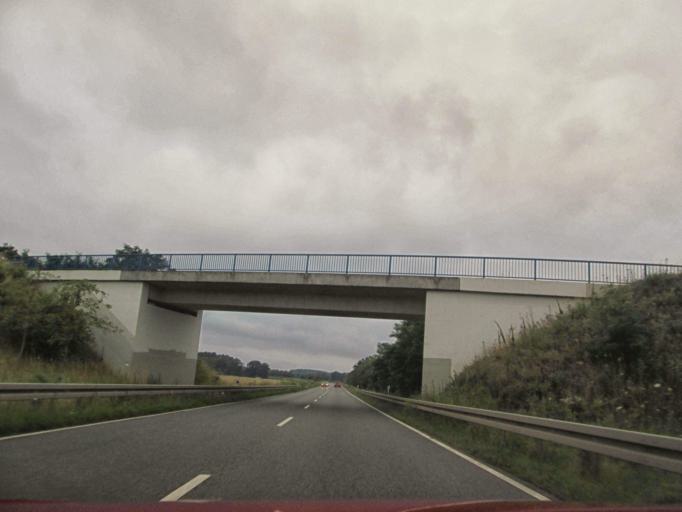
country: DE
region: Lower Saxony
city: Osloss
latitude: 52.4246
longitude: 10.6857
